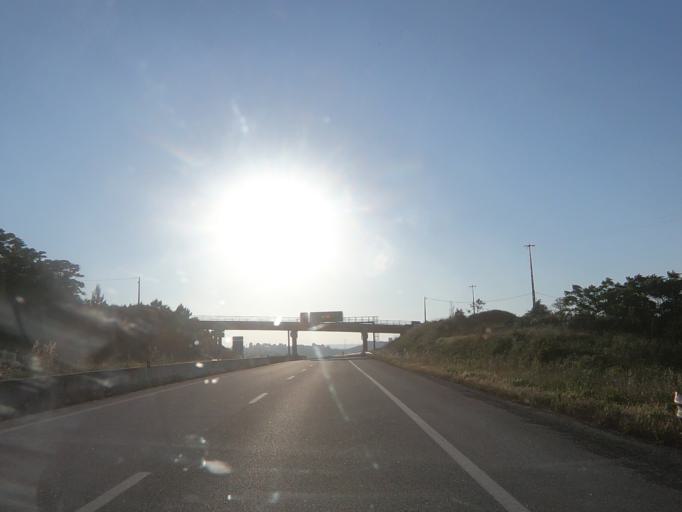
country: PT
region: Guarda
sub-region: Celorico da Beira
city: Celorico da Beira
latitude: 40.6269
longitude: -7.3688
